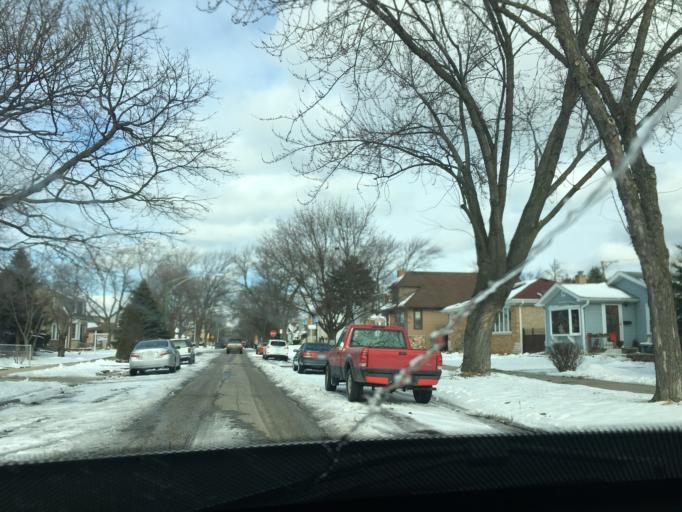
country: US
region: Illinois
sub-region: Cook County
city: Elmwood Park
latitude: 41.9354
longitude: -87.8128
